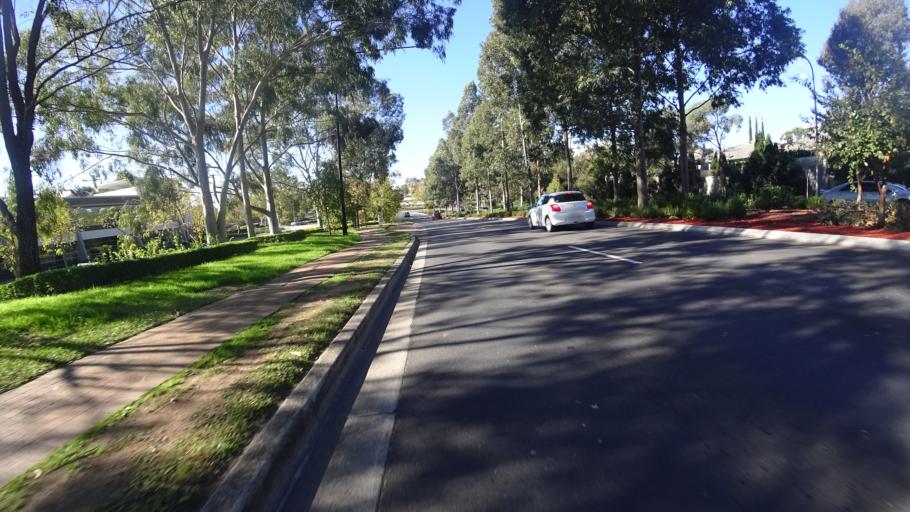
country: AU
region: New South Wales
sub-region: Blacktown
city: Stanhope Gardens
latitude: -33.7371
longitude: 150.9592
